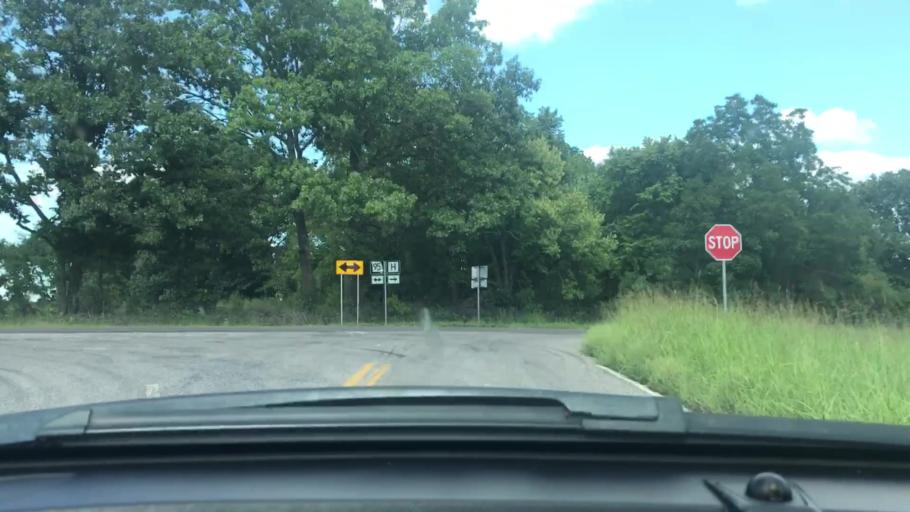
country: US
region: Missouri
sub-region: Wright County
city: Hartville
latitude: 37.3795
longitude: -92.3629
